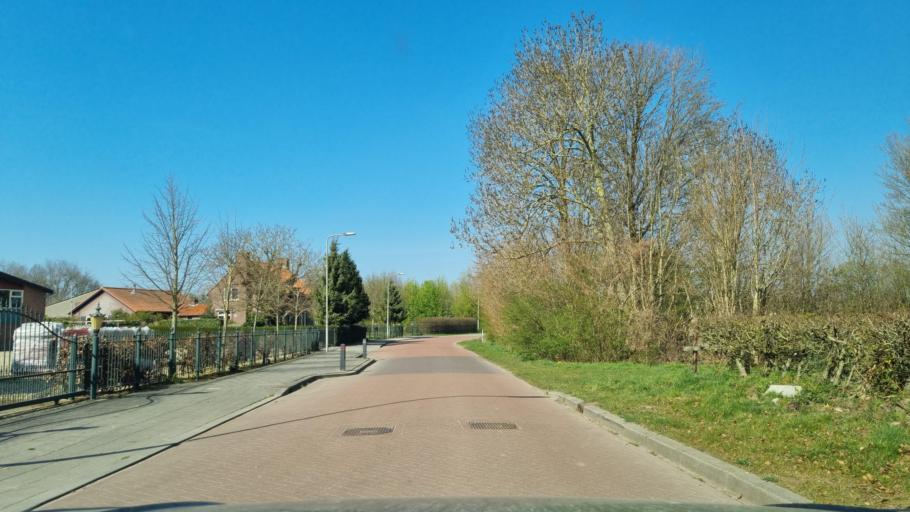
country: NL
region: Limburg
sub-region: Gemeente Gennep
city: Gennep
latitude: 51.7170
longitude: 6.0255
